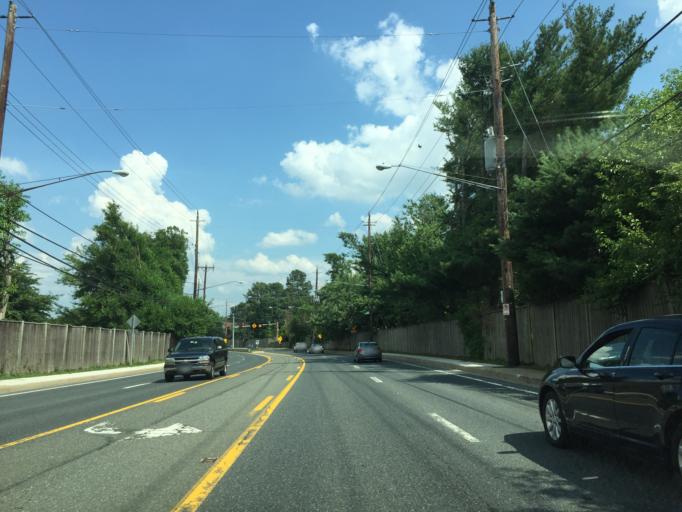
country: US
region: Maryland
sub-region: Montgomery County
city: Colesville
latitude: 39.0672
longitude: -76.9851
